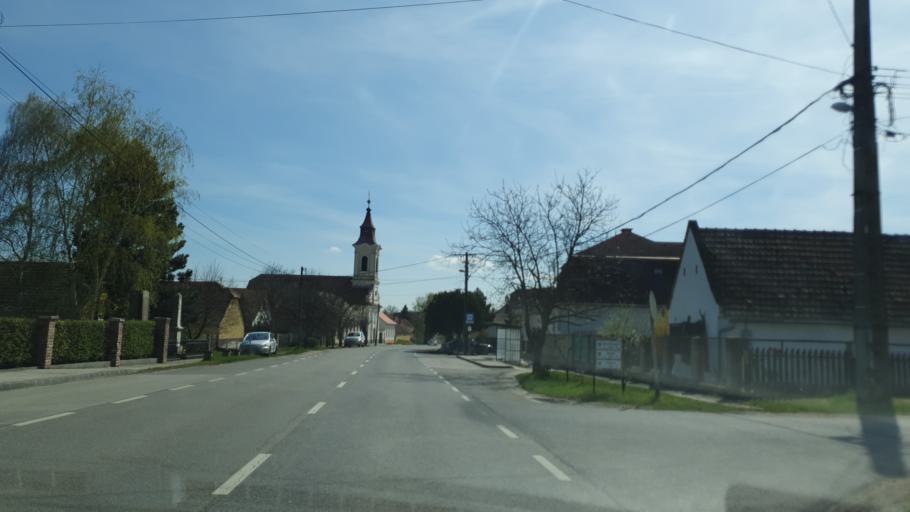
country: HU
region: Fejer
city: Pusztavam
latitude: 47.4385
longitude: 18.2334
